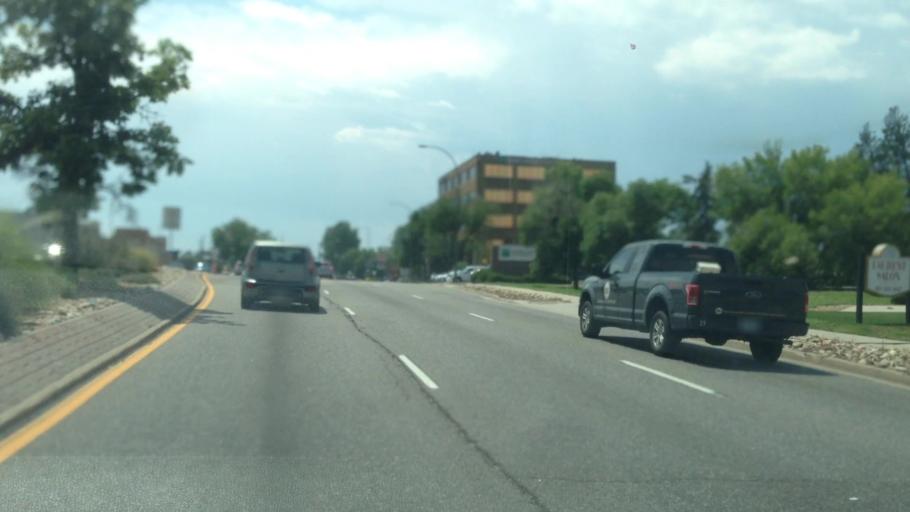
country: US
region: Colorado
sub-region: Jefferson County
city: Lakewood
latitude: 39.7137
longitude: -105.0816
